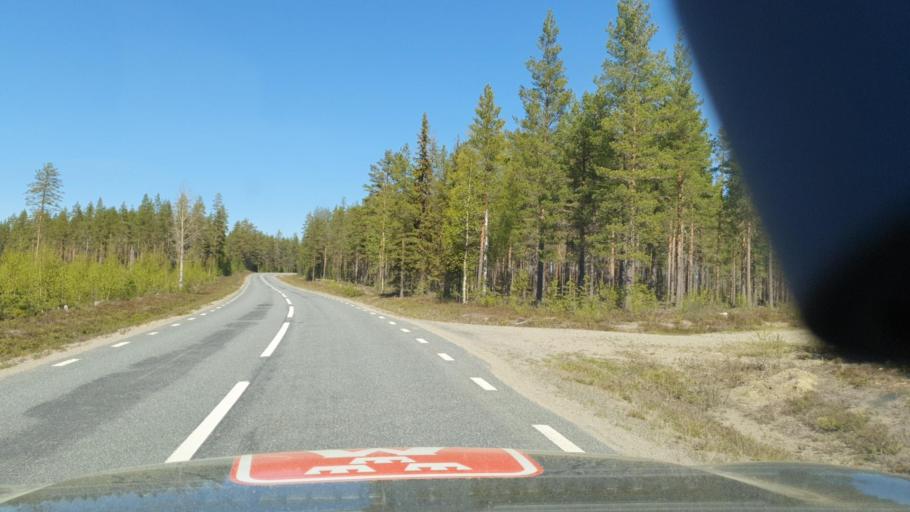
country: SE
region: Vaesternorrland
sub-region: OErnskoeldsviks Kommun
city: Bredbyn
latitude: 63.8353
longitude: 18.4785
